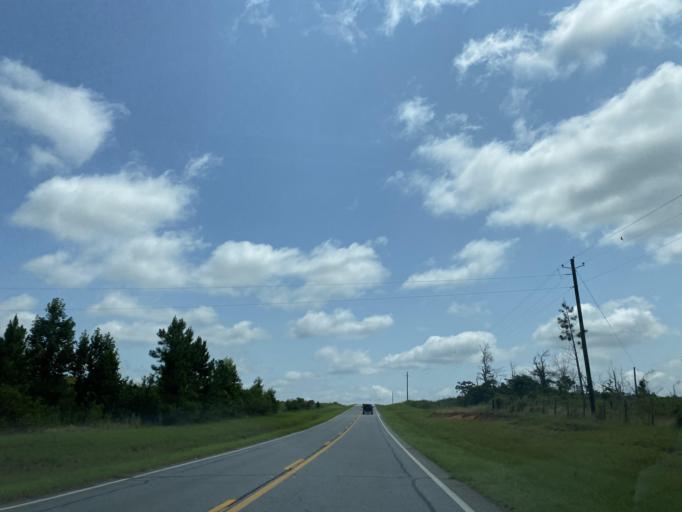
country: US
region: Georgia
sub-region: Telfair County
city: Helena
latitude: 32.0141
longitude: -83.0876
